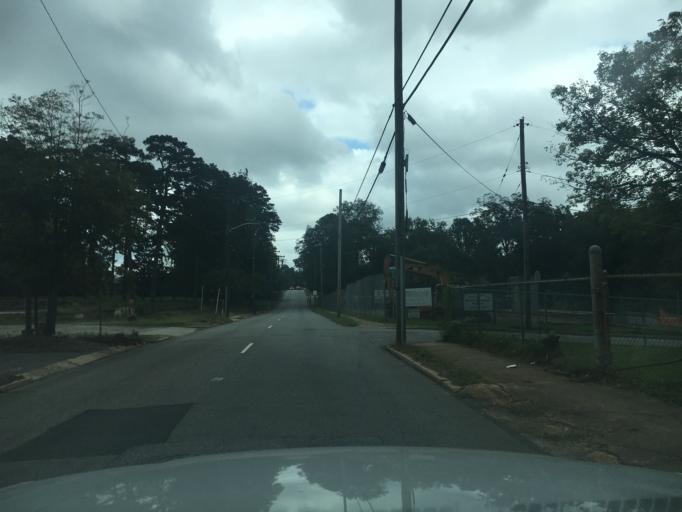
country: US
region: North Carolina
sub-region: Catawba County
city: Hickory
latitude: 35.7299
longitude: -81.3373
